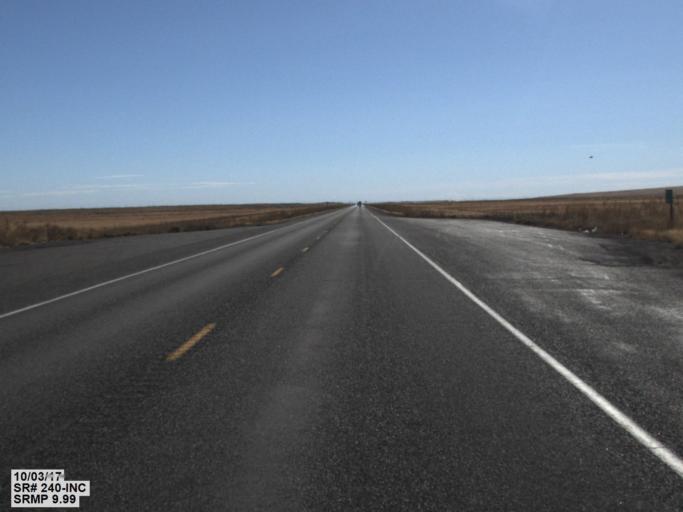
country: US
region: Washington
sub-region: Benton County
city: Benton City
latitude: 46.4858
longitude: -119.5812
